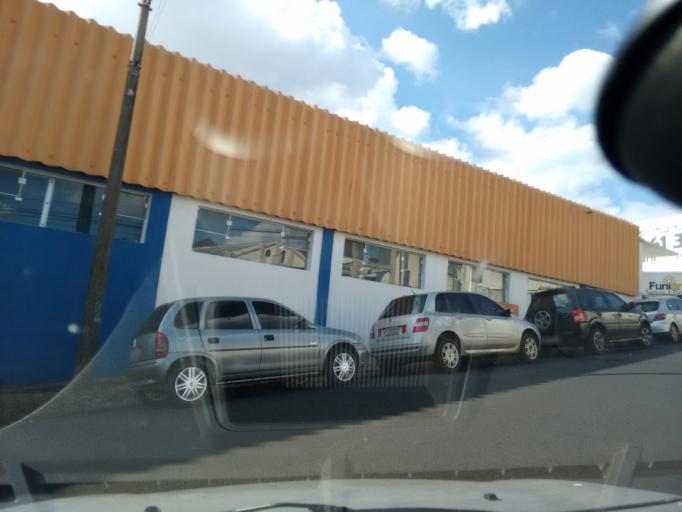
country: BR
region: Sao Paulo
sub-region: Araraquara
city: Araraquara
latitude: -21.7951
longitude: -48.1720
